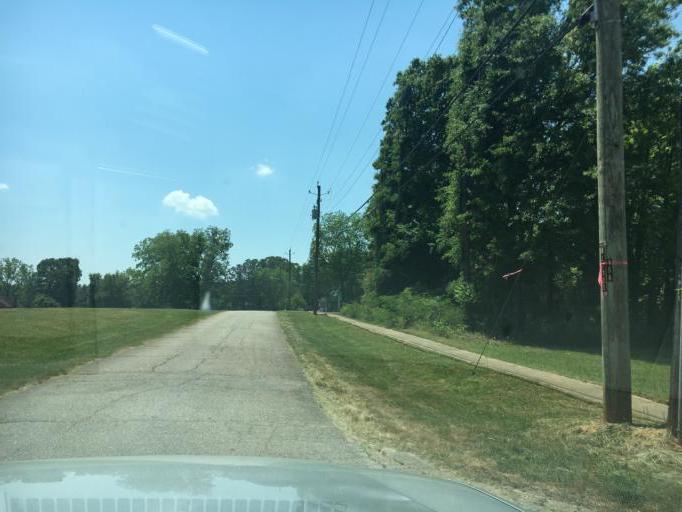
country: US
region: Georgia
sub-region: Franklin County
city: Lavonia
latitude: 34.3713
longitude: -83.0843
